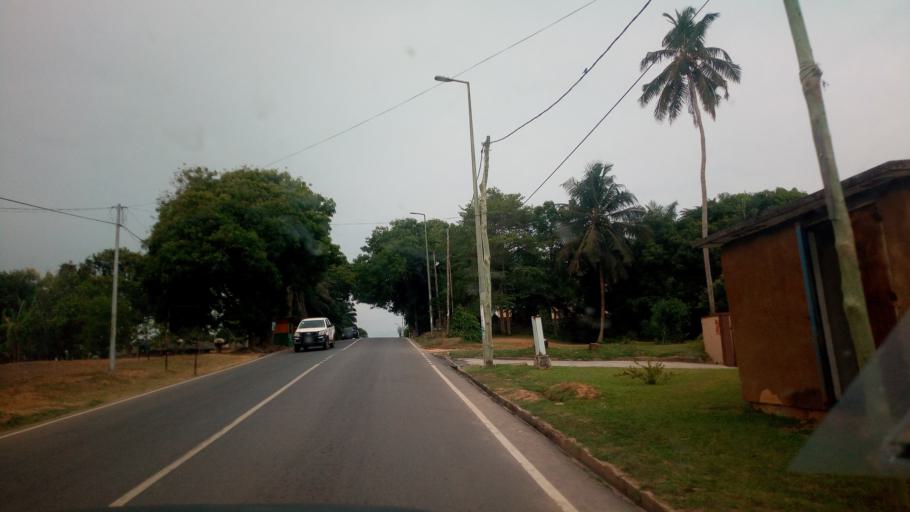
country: GH
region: Western
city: Takoradi
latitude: 4.8807
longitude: -1.7592
